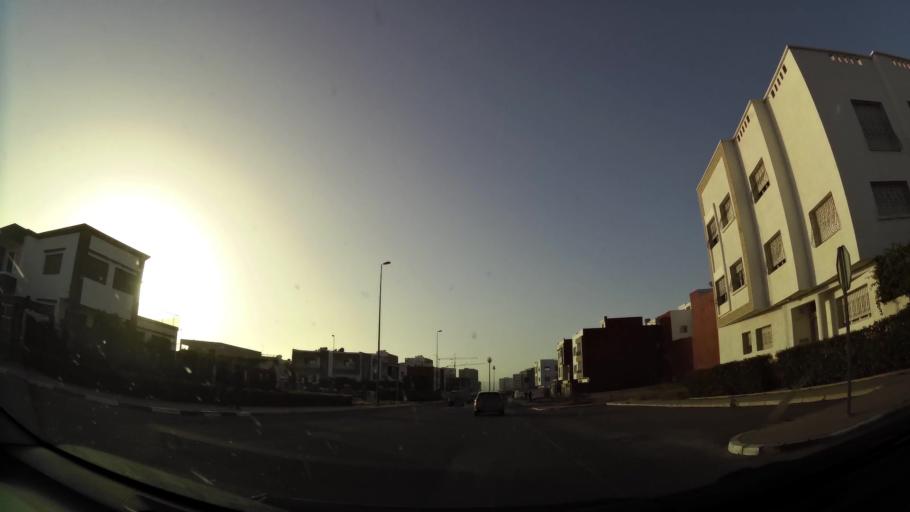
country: MA
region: Oued ed Dahab-Lagouira
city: Dakhla
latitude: 30.3965
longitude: -9.5753
